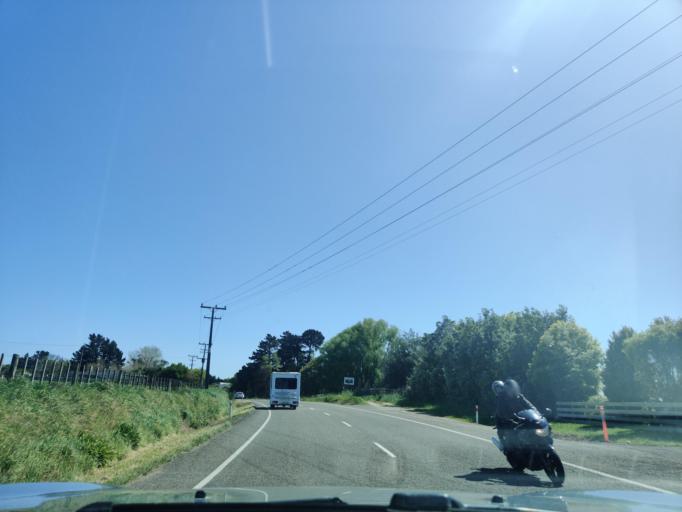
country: NZ
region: Manawatu-Wanganui
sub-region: Wanganui District
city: Wanganui
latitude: -39.8800
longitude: 175.0020
